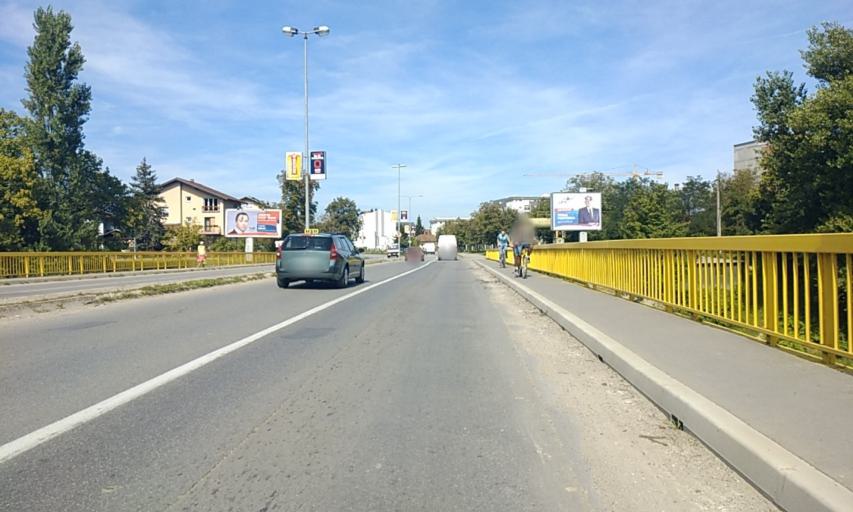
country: BA
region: Republika Srpska
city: Starcevica
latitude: 44.7677
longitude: 17.2099
